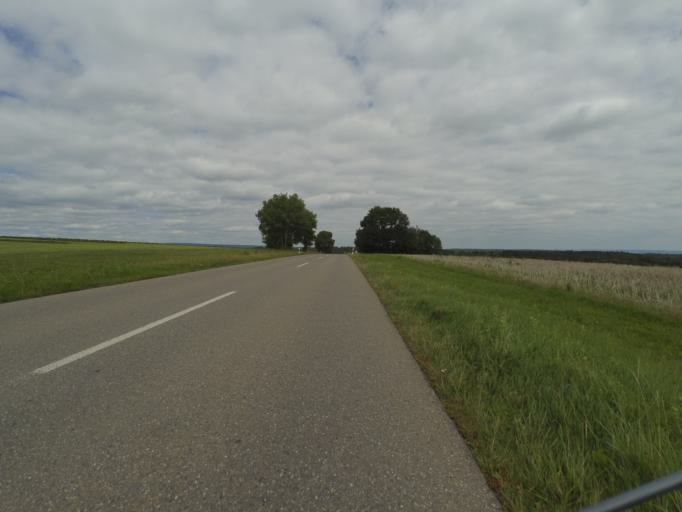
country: DE
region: Baden-Wuerttemberg
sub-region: Freiburg Region
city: Loffingen
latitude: 47.8630
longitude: 8.3491
